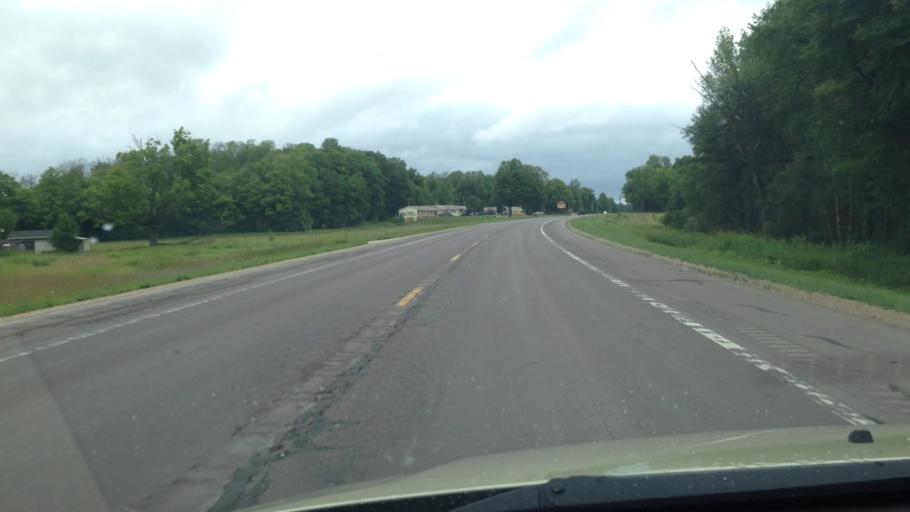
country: US
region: Michigan
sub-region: Schoolcraft County
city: Manistique
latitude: 46.0817
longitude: -85.9573
